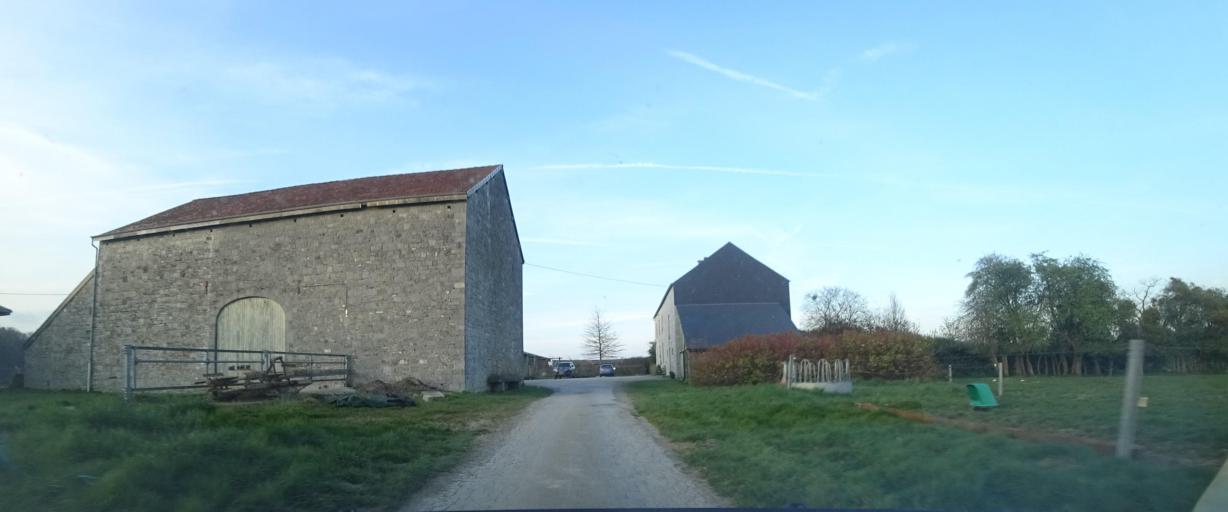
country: BE
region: Wallonia
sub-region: Province de Namur
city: Havelange
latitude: 50.3385
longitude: 5.2203
